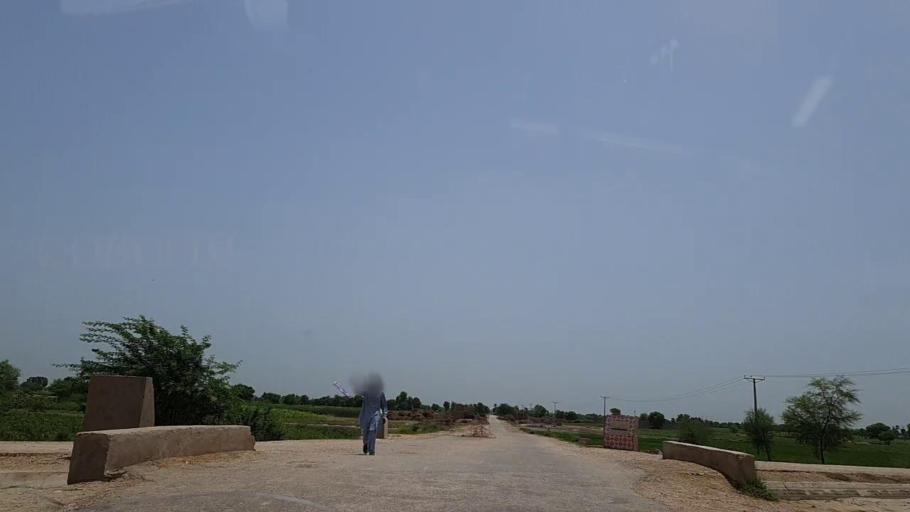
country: PK
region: Sindh
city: Tharu Shah
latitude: 26.9567
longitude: 68.0750
